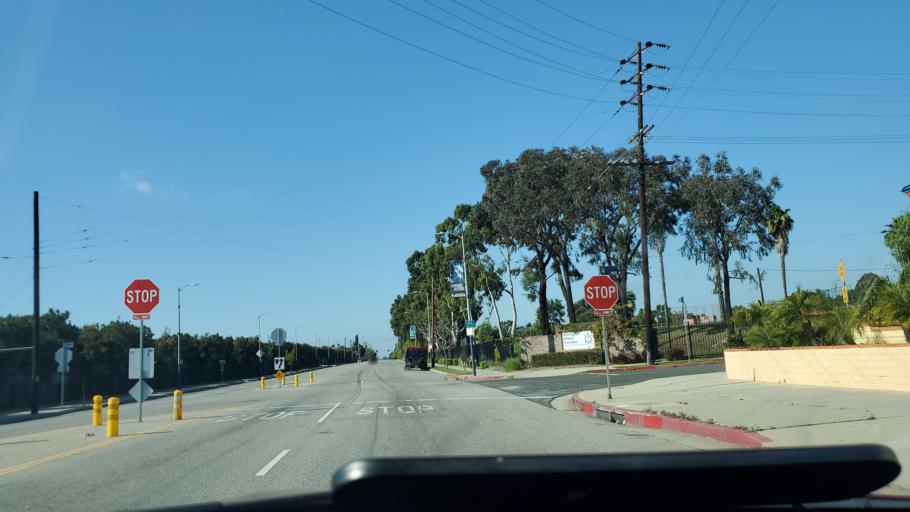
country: US
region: California
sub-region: Los Angeles County
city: West Carson
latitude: 33.7937
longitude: -118.2823
